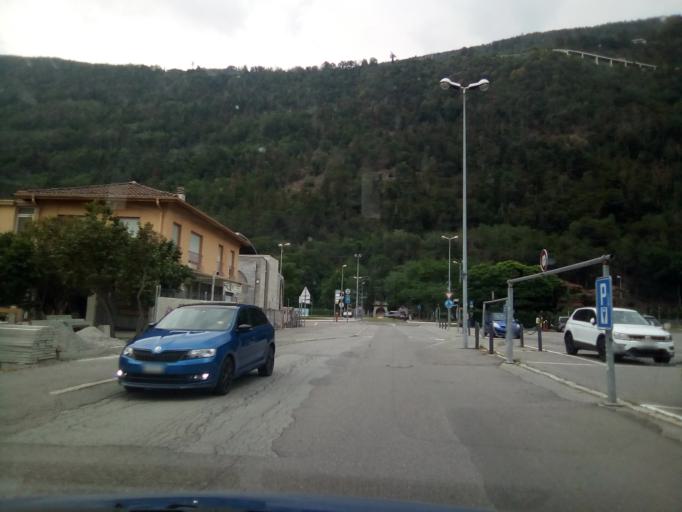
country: CH
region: Valais
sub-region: Martigny District
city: Martigny-Ville
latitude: 46.0975
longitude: 7.0764
